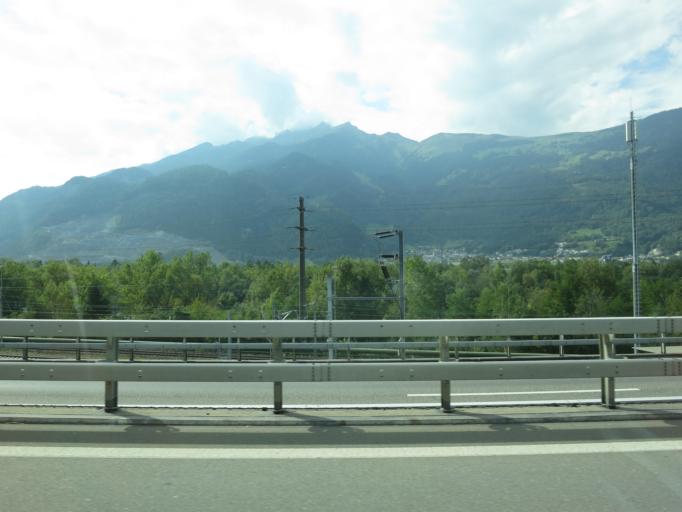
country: CH
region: Grisons
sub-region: Landquart District
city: Zizers
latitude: 46.9305
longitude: 9.5604
